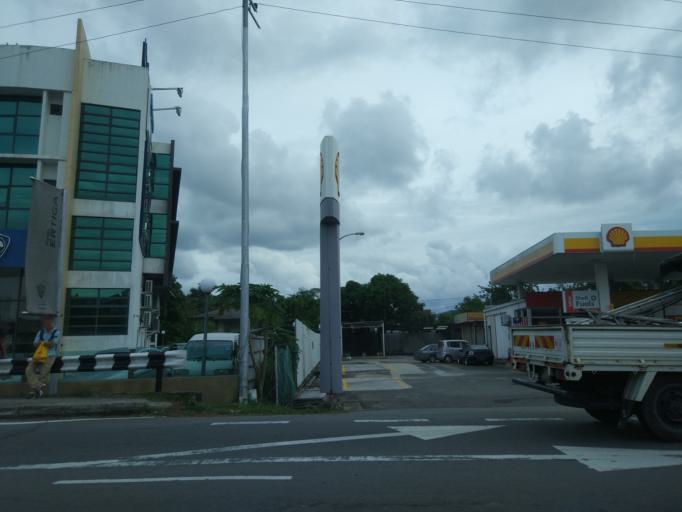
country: MY
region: Sabah
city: Kota Kinabalu
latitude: 5.9769
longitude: 116.0967
